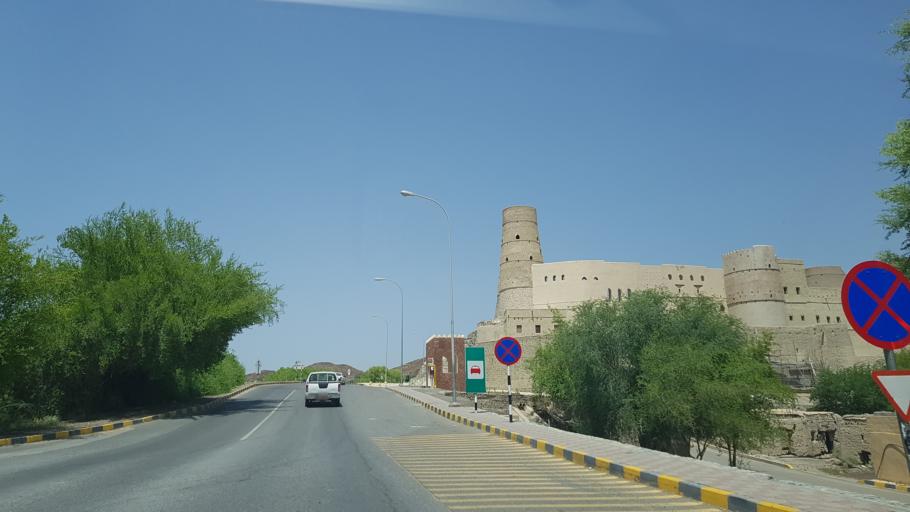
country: OM
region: Muhafazat ad Dakhiliyah
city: Bahla'
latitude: 22.9638
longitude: 57.2995
